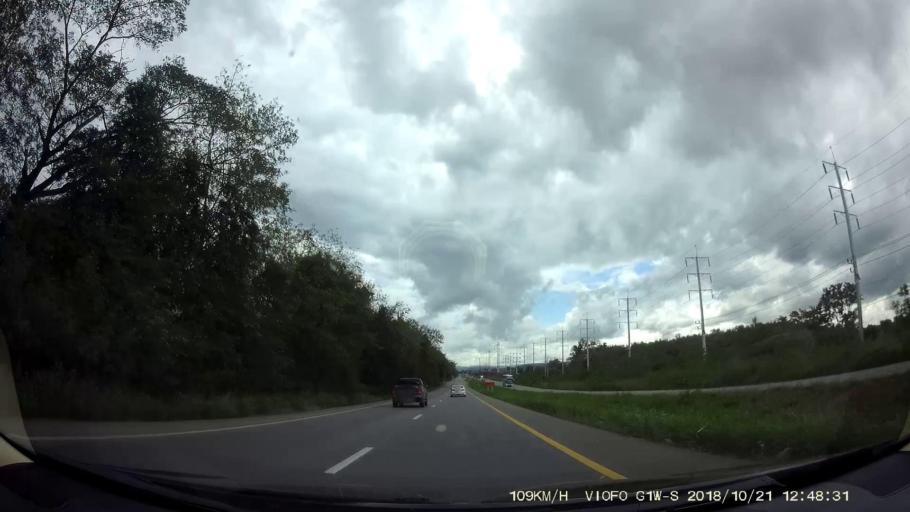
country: TH
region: Nakhon Ratchasima
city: Amphoe Sikhiu
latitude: 14.9111
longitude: 101.6840
